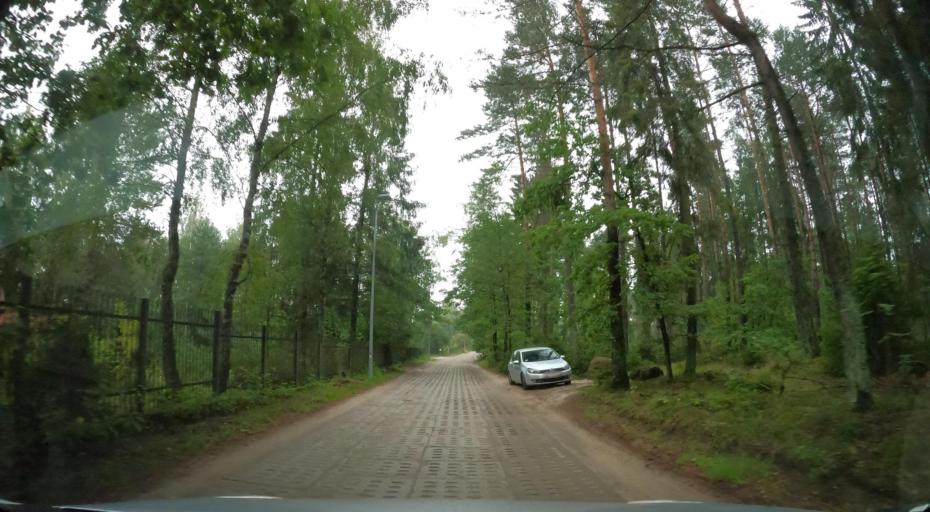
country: PL
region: Pomeranian Voivodeship
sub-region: Powiat kartuski
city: Chwaszczyno
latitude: 54.4181
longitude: 18.4295
